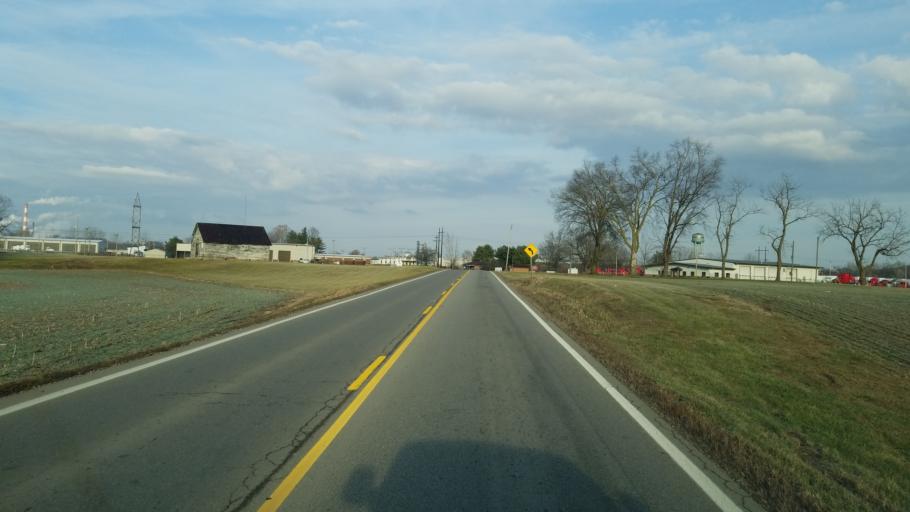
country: US
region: Ohio
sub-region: Ross County
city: Chillicothe
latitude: 39.3178
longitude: -82.9458
